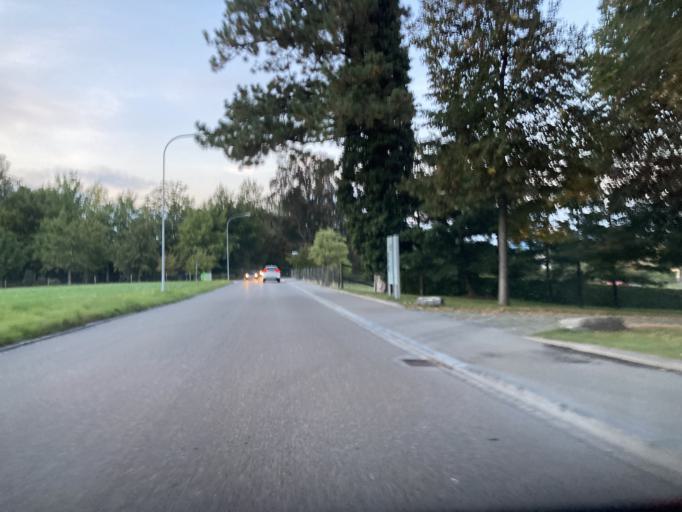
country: CH
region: Zurich
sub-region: Bezirk Horgen
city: Ruschlikon
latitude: 47.3131
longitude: 8.5465
